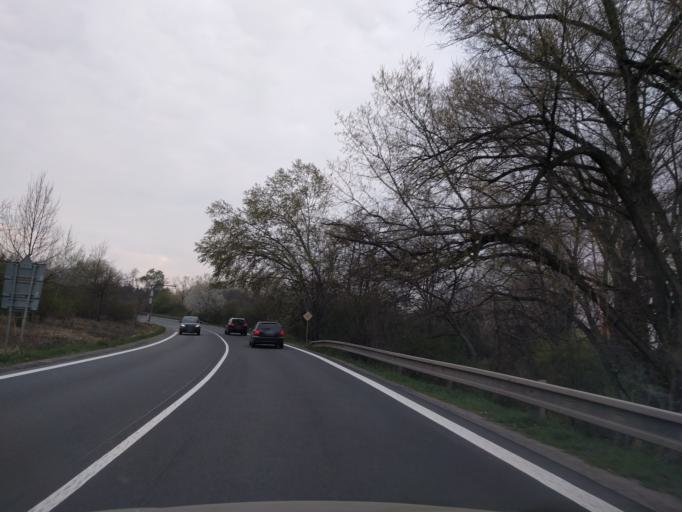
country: CZ
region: Central Bohemia
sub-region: Okres Praha-Vychod
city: Ricany
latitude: 49.9986
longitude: 14.6539
